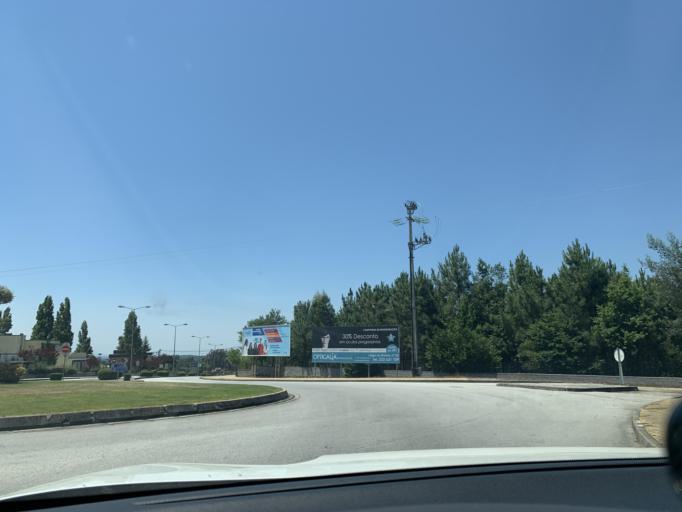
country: PT
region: Viseu
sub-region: Mangualde
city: Mangualde
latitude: 40.5928
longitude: -7.7590
